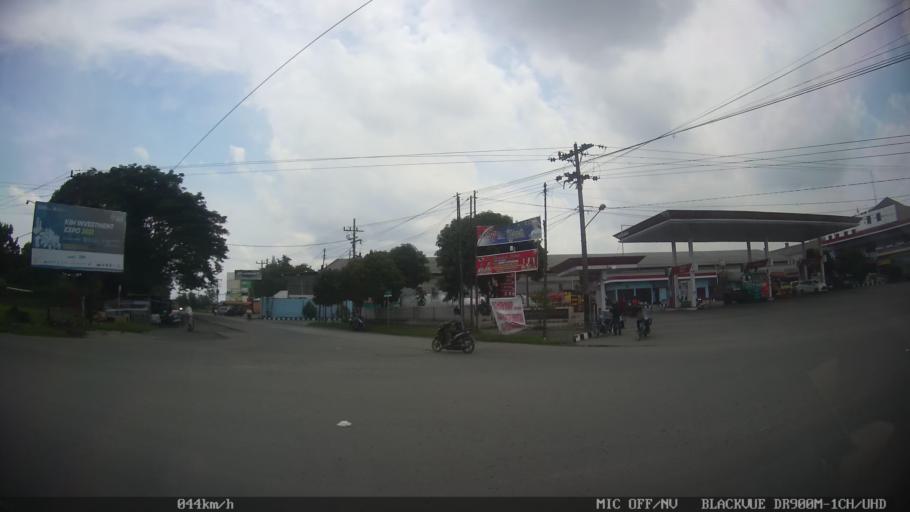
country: ID
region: North Sumatra
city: Labuhan Deli
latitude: 3.6734
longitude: 98.6765
